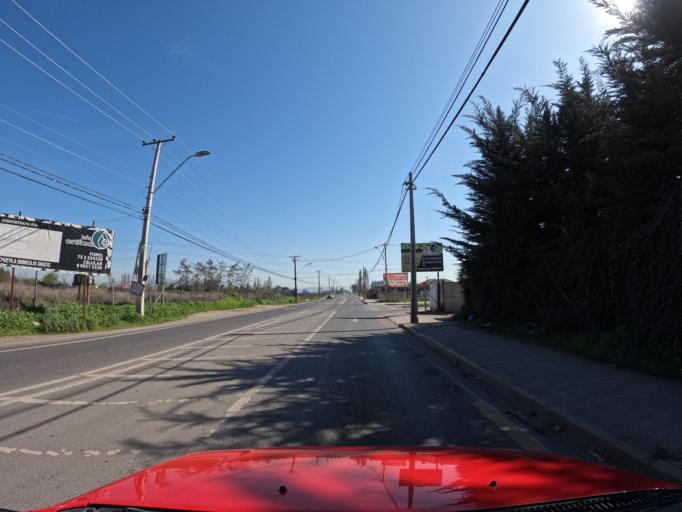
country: CL
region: Maule
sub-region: Provincia de Curico
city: Curico
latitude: -34.9615
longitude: -71.2504
